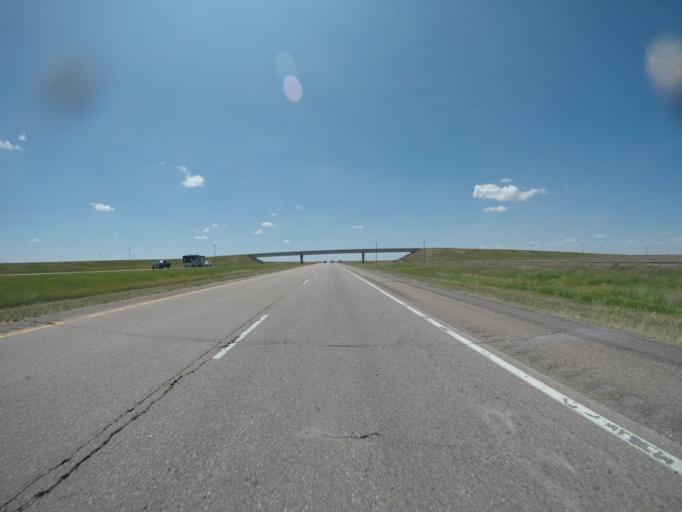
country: US
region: Colorado
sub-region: Lincoln County
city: Hugo
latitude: 39.2816
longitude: -103.3394
